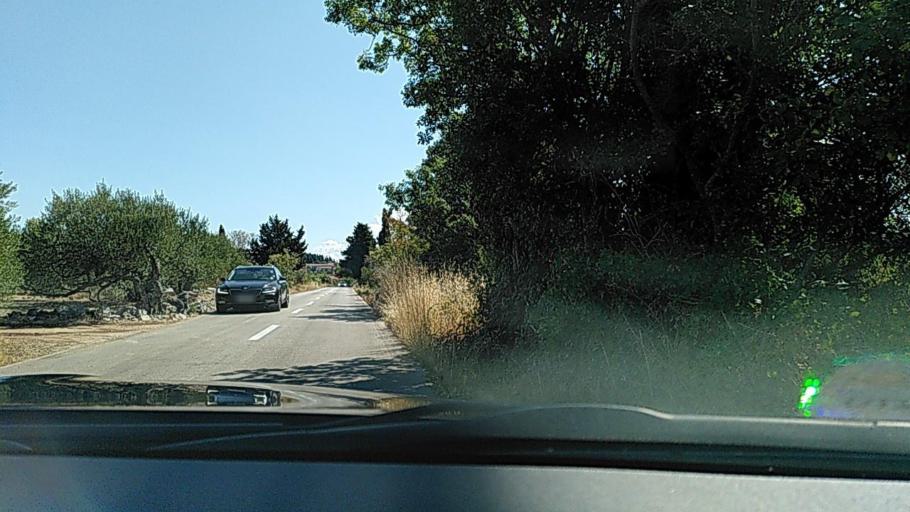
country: HR
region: Splitsko-Dalmatinska
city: Tucepi
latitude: 43.1308
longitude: 16.9907
